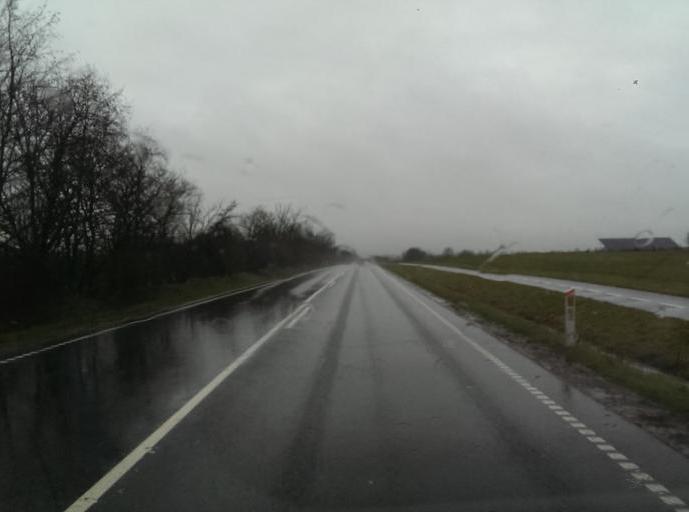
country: DK
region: South Denmark
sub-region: Varde Kommune
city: Olgod
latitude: 55.7264
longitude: 8.6131
